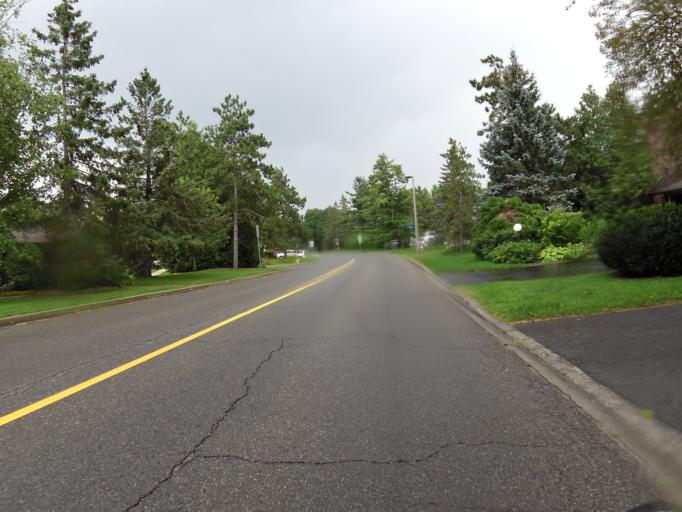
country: CA
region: Ontario
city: Bells Corners
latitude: 45.3308
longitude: -75.9111
